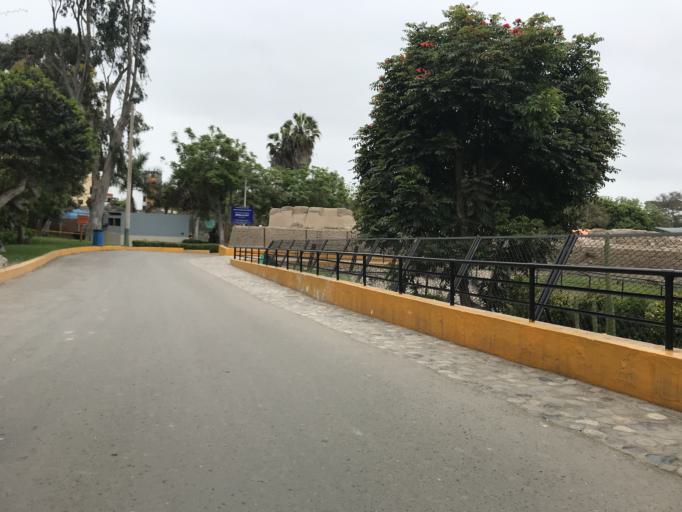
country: PE
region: Callao
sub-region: Callao
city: Callao
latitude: -12.0705
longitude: -77.0876
